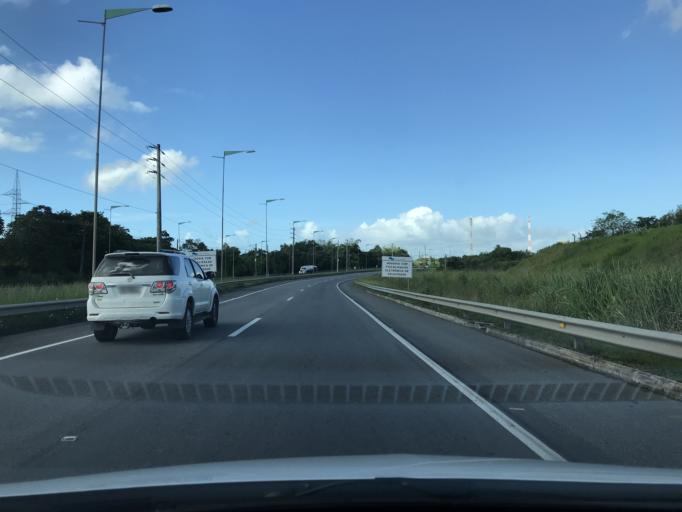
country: BR
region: Pernambuco
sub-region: Ipojuca
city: Ipojuca
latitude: -8.3789
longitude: -35.0078
